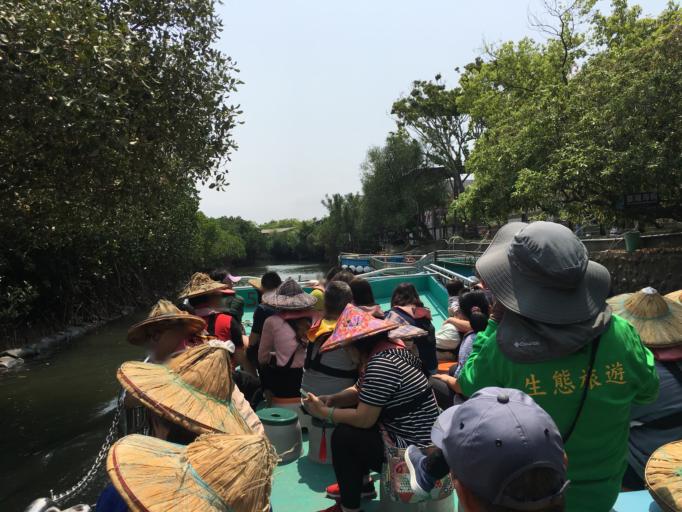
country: TW
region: Taiwan
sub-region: Tainan
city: Tainan
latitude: 23.0203
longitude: 120.1353
